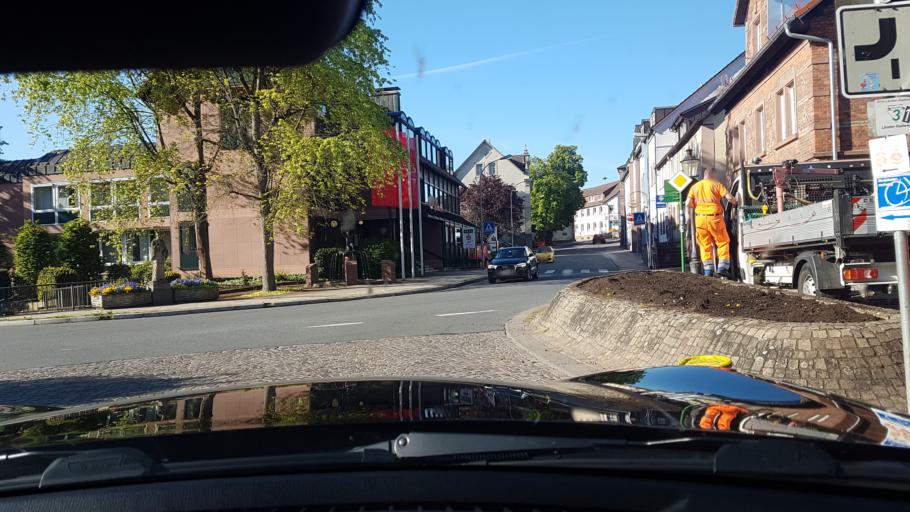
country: DE
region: Baden-Wuerttemberg
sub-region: Karlsruhe Region
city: Buchen
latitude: 49.5213
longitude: 9.3232
